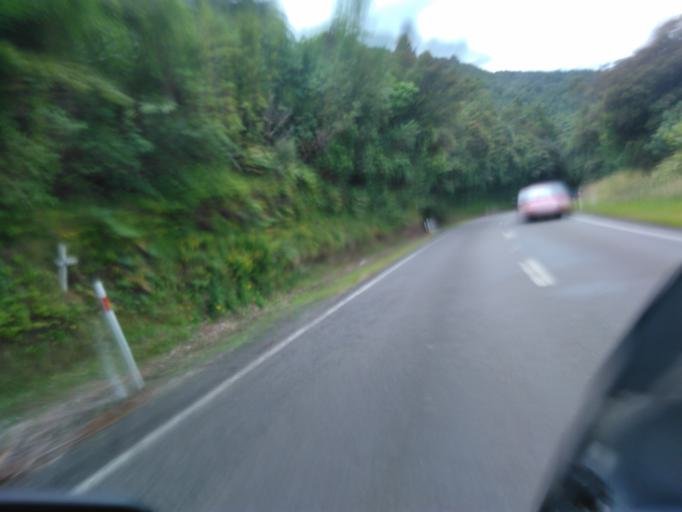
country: NZ
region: Bay of Plenty
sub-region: Opotiki District
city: Opotiki
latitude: -38.2300
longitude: 177.3110
